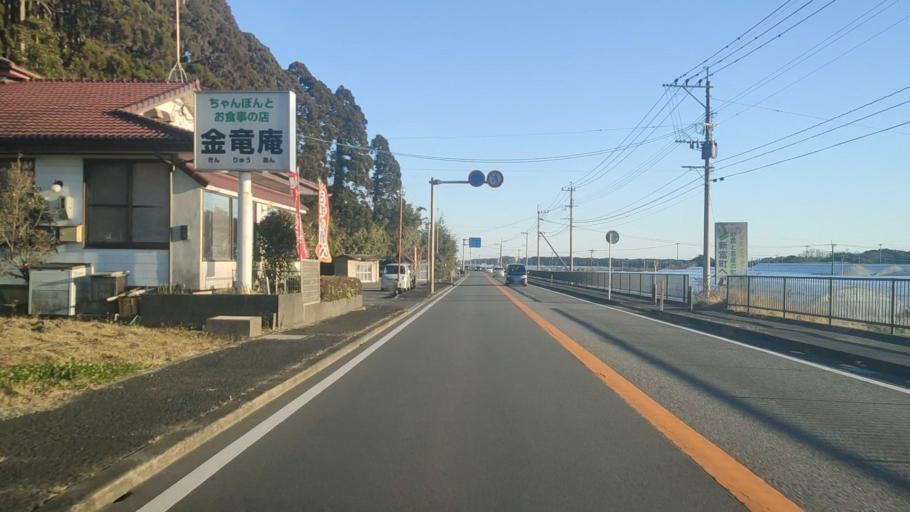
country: JP
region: Miyazaki
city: Takanabe
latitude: 32.0894
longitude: 131.5134
